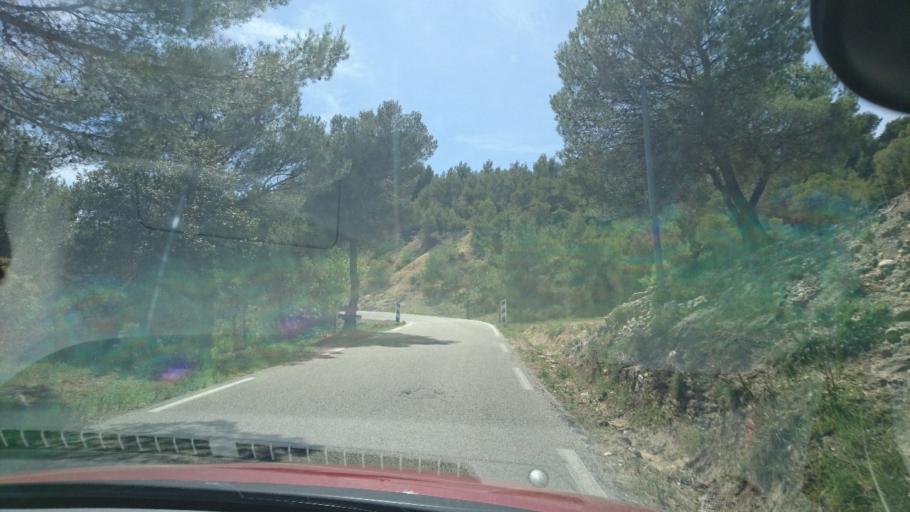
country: FR
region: Provence-Alpes-Cote d'Azur
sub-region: Departement du Vaucluse
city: Bedoin
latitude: 44.1371
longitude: 5.1475
